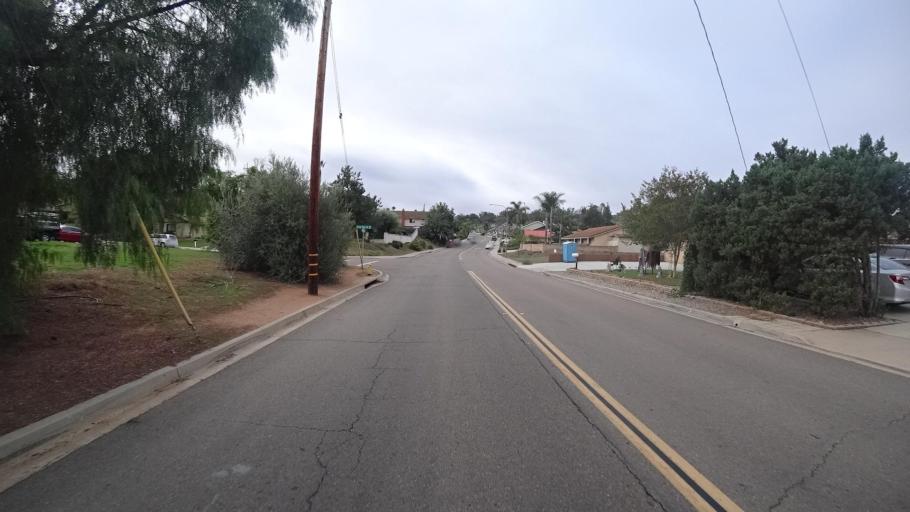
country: US
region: California
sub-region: San Diego County
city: Rancho San Diego
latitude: 32.7570
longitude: -116.9180
